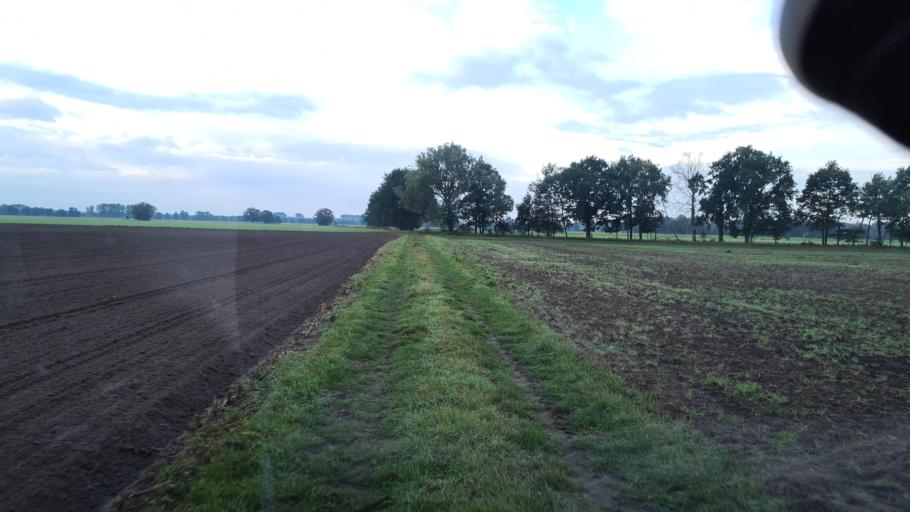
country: DE
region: Brandenburg
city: Schonewalde
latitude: 51.6832
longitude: 13.5697
